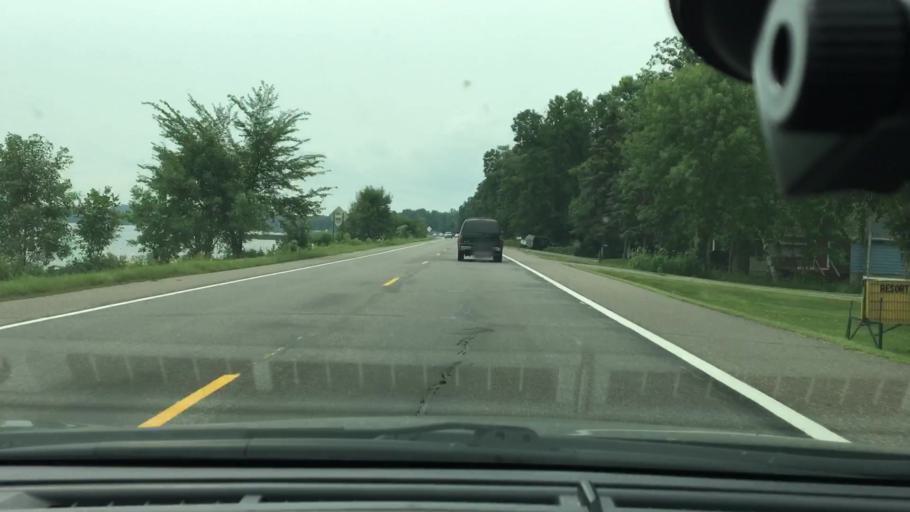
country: US
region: Minnesota
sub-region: Mille Lacs County
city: Vineland
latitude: 46.2647
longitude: -93.8243
